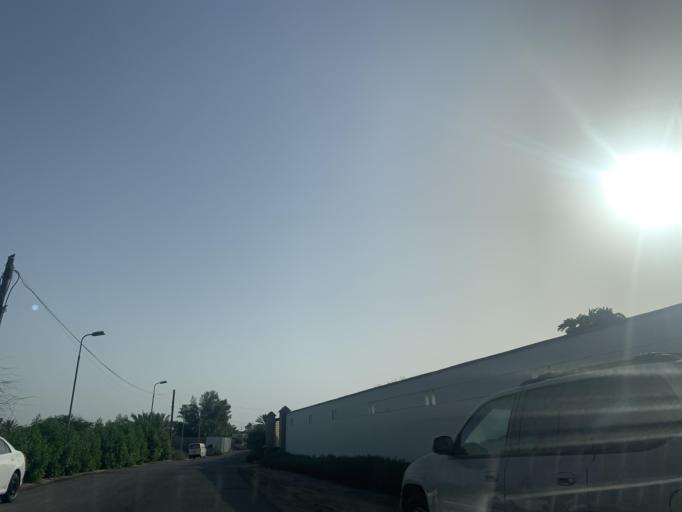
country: BH
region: Northern
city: Madinat `Isa
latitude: 26.1899
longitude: 50.4630
